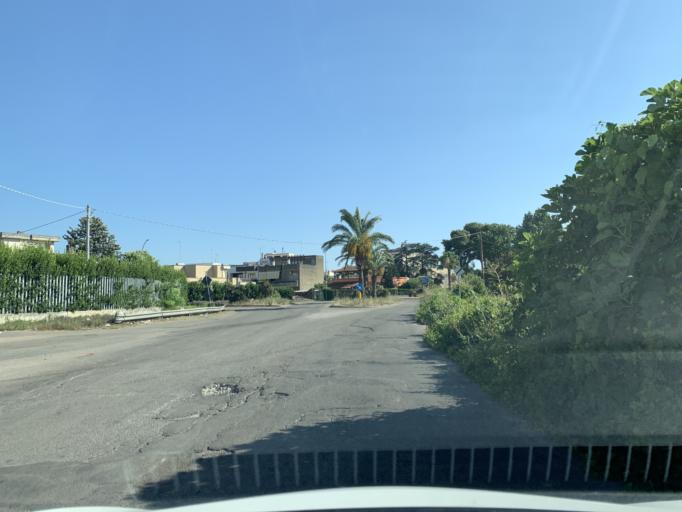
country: IT
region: Apulia
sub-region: Provincia di Lecce
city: Nardo
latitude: 40.1857
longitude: 18.0390
